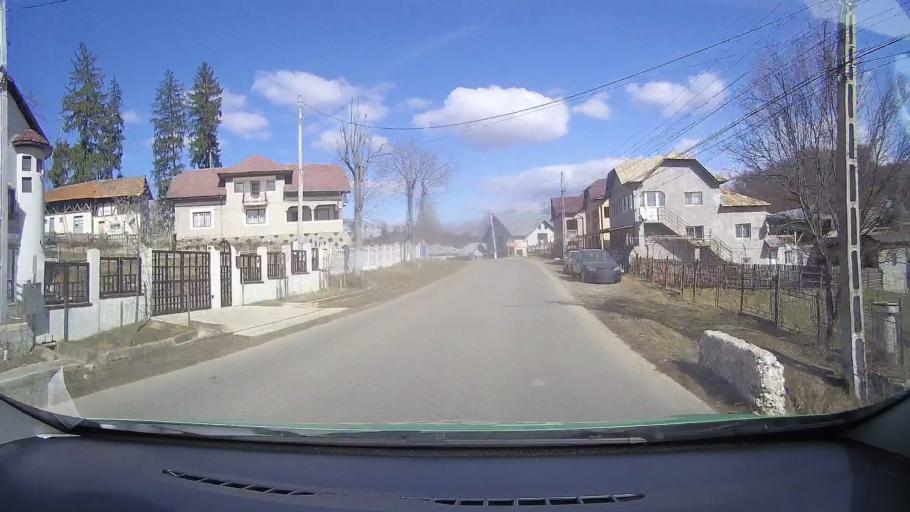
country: RO
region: Dambovita
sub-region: Comuna Vulcana Bai
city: Vulcana Bai
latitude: 45.0684
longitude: 25.3784
